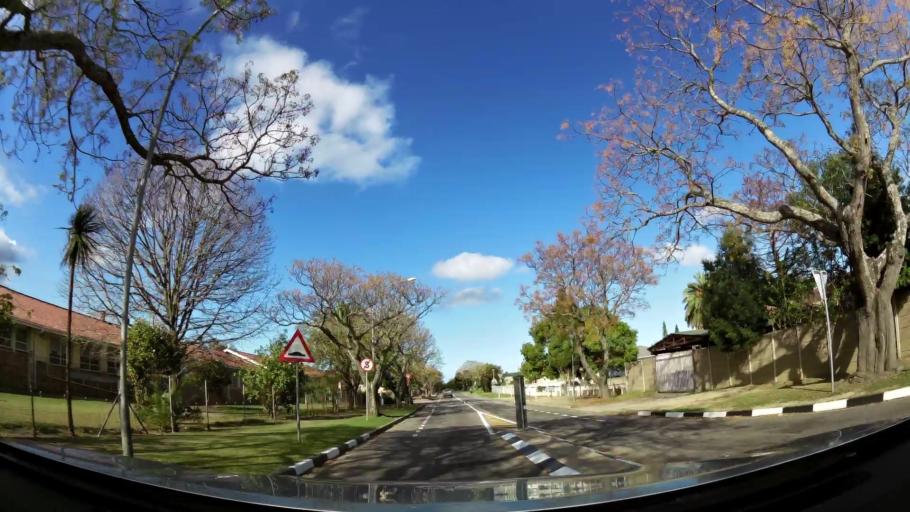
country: ZA
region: Western Cape
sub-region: Eden District Municipality
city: George
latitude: -33.9576
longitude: 22.4752
